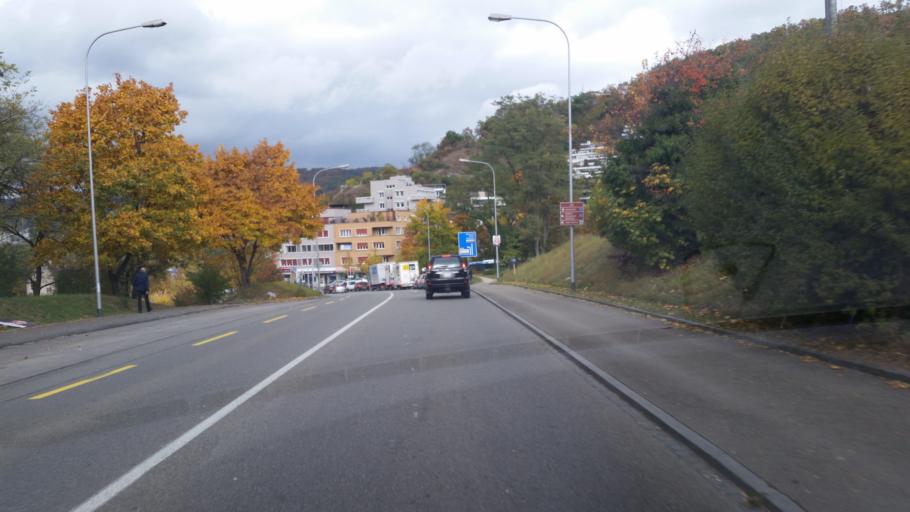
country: CH
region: Aargau
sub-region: Bezirk Baden
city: Wettingen
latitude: 47.4702
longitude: 8.3123
